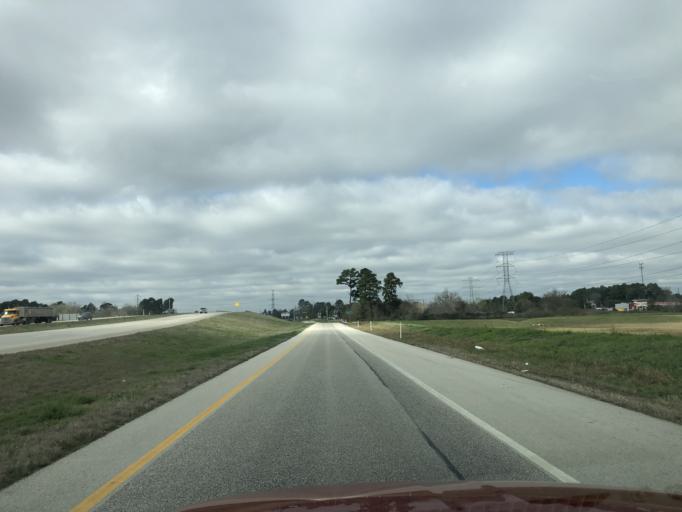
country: US
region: Texas
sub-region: Montgomery County
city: The Woodlands
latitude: 30.0947
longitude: -95.5028
